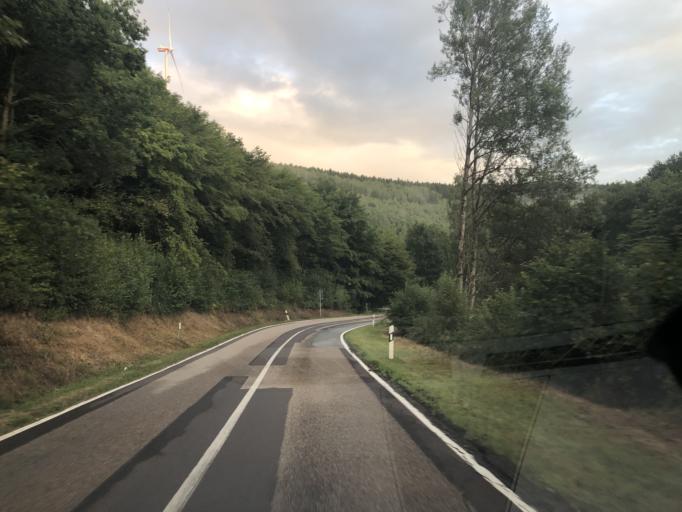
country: DE
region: Rheinland-Pfalz
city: Grimburg
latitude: 49.6025
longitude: 6.8776
